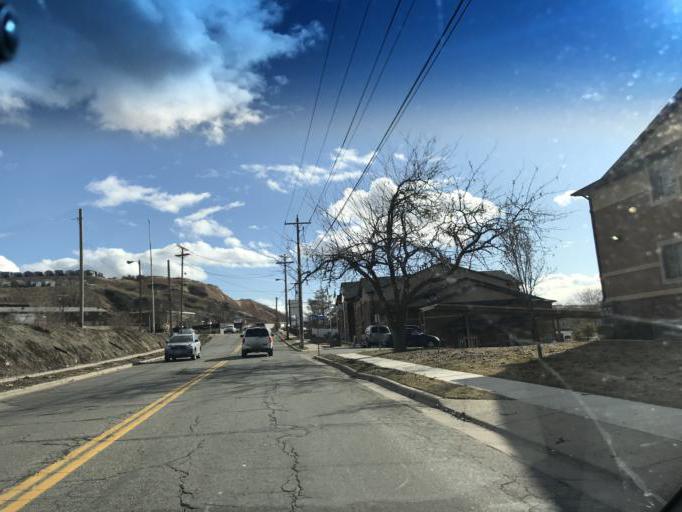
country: US
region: Utah
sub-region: Davis County
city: North Salt Lake
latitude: 40.8402
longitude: -111.9118
